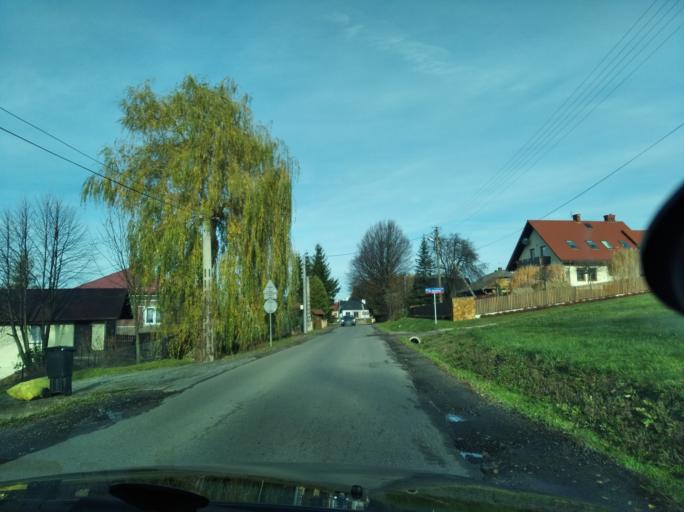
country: PL
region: Subcarpathian Voivodeship
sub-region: Powiat rzeszowski
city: Tyczyn
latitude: 49.9957
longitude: 22.0672
